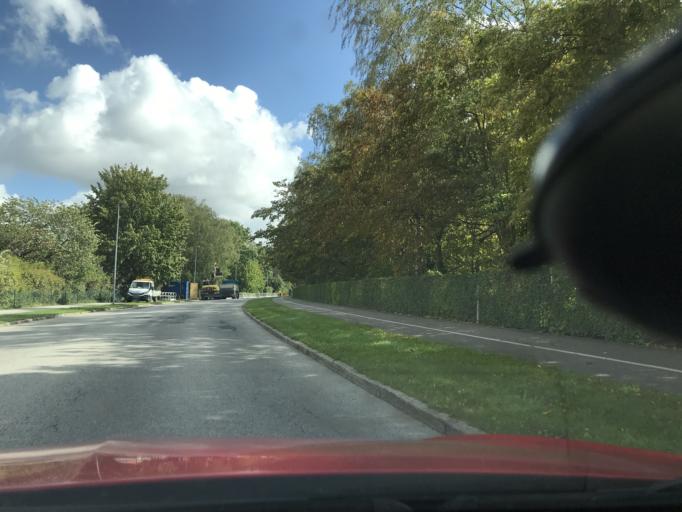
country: SE
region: Skane
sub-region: Lunds Kommun
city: Lund
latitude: 55.7168
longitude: 13.1957
